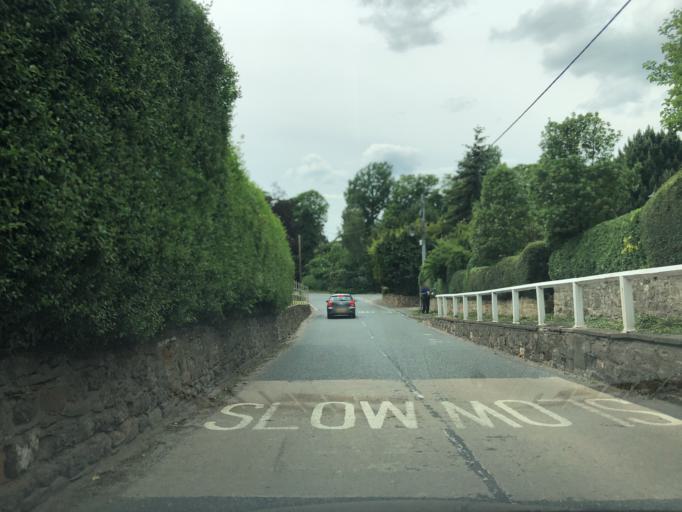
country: GB
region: England
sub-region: North Yorkshire
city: Angram Grange
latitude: 54.2366
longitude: -1.2617
